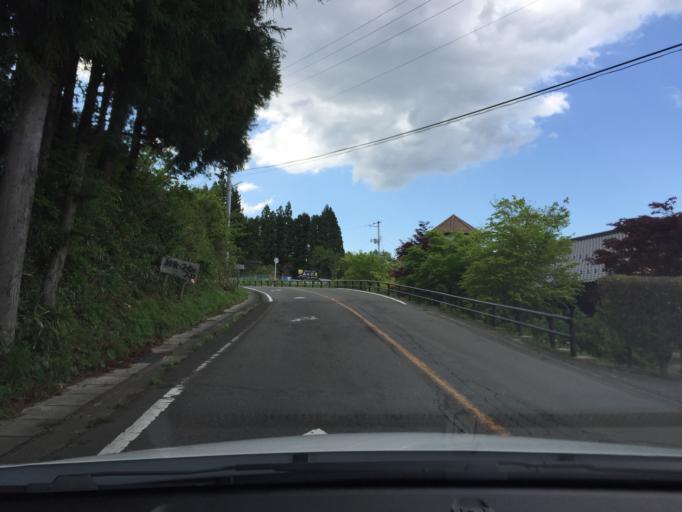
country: JP
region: Fukushima
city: Fukushima-shi
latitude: 37.7559
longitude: 140.3557
